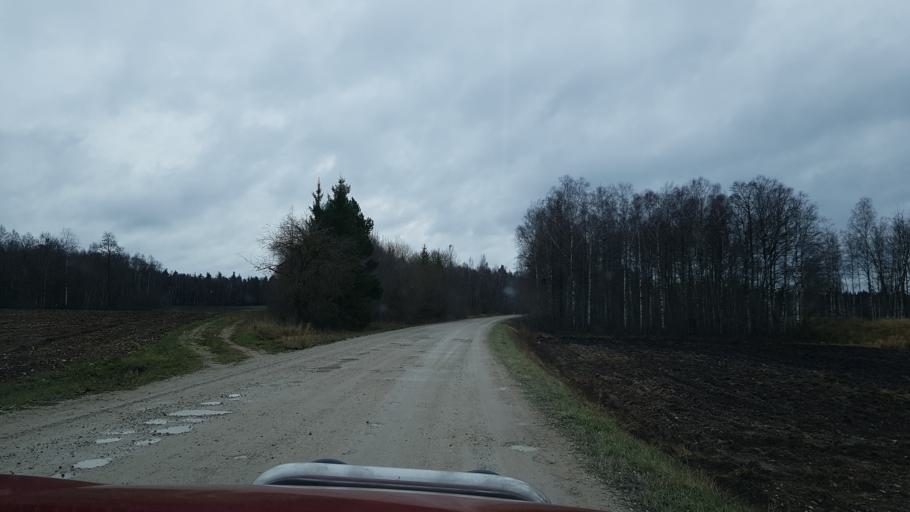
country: EE
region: Paernumaa
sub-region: Halinga vald
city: Parnu-Jaagupi
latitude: 58.5615
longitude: 24.4134
